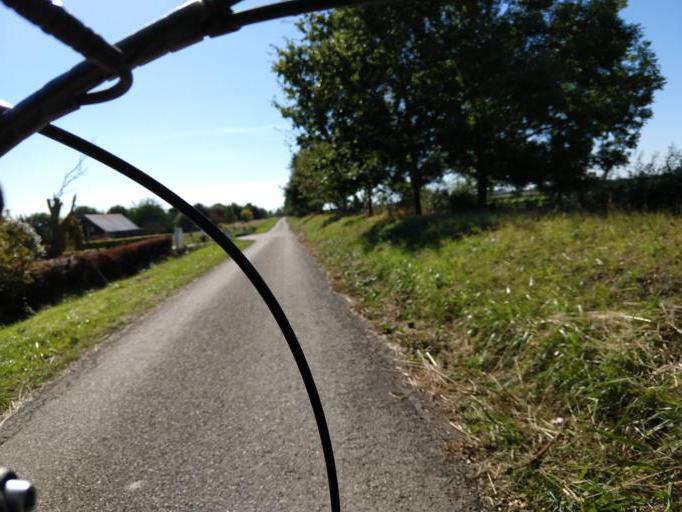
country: NL
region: Zeeland
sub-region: Gemeente Terneuzen
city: Terneuzen
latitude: 51.3980
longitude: 3.8490
